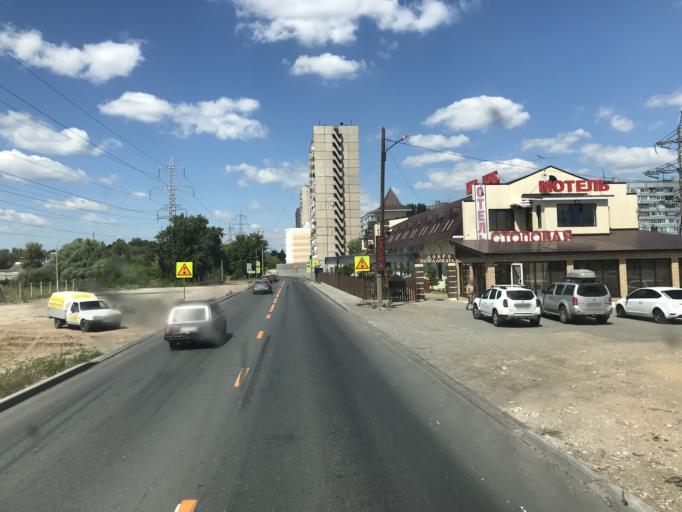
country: RU
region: Samara
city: Zhigulevsk
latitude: 53.4698
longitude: 49.5129
